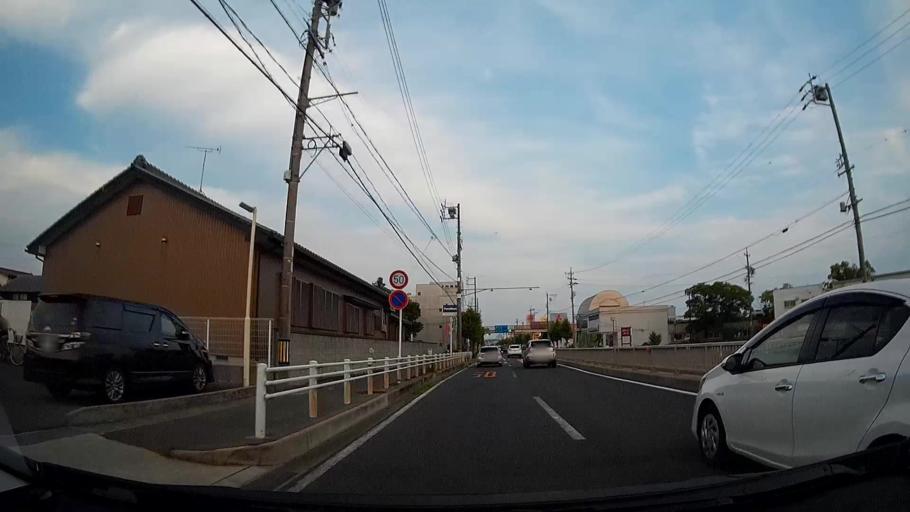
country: JP
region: Aichi
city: Kozakai-cho
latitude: 34.7875
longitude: 137.3763
